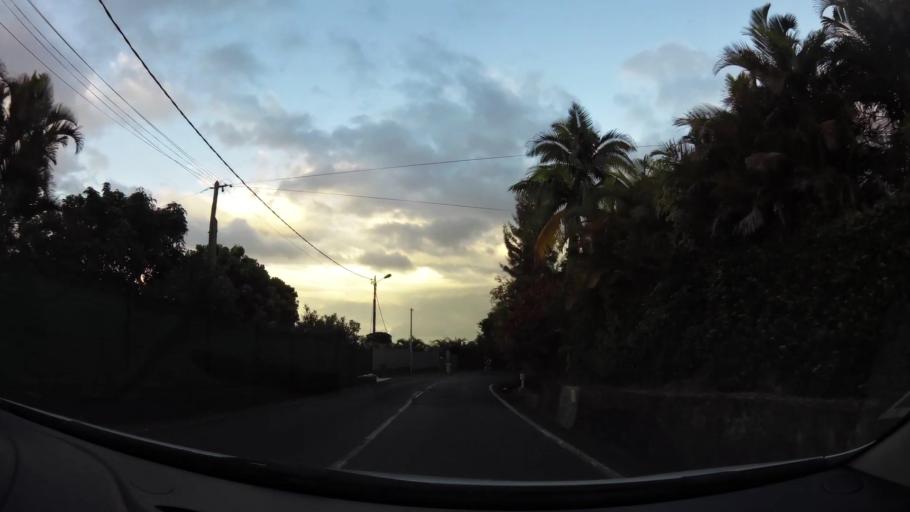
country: RE
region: Reunion
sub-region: Reunion
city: Saint-Denis
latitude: -20.9154
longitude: 55.4607
